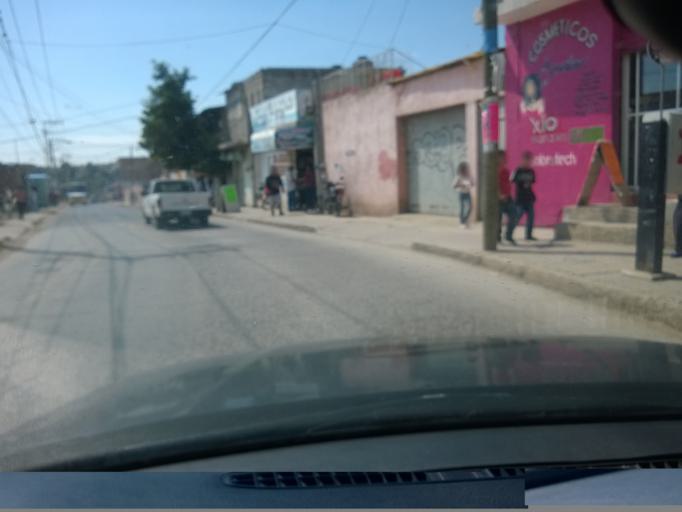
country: MX
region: Guanajuato
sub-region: Leon
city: Centro Familiar la Soledad
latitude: 21.1364
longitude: -101.7454
